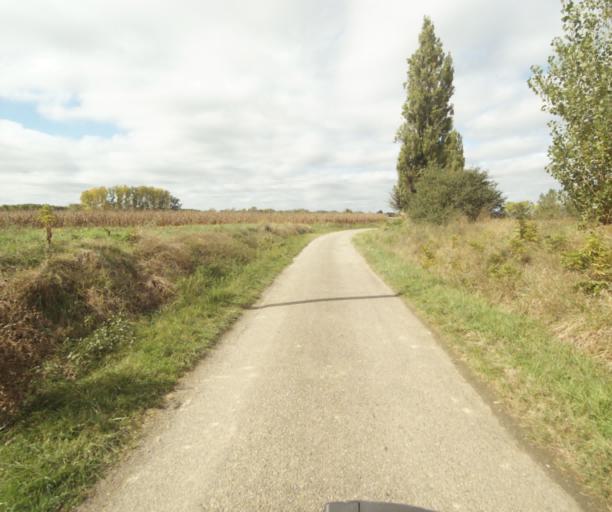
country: FR
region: Midi-Pyrenees
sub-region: Departement du Tarn-et-Garonne
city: Finhan
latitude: 43.9160
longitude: 1.2126
